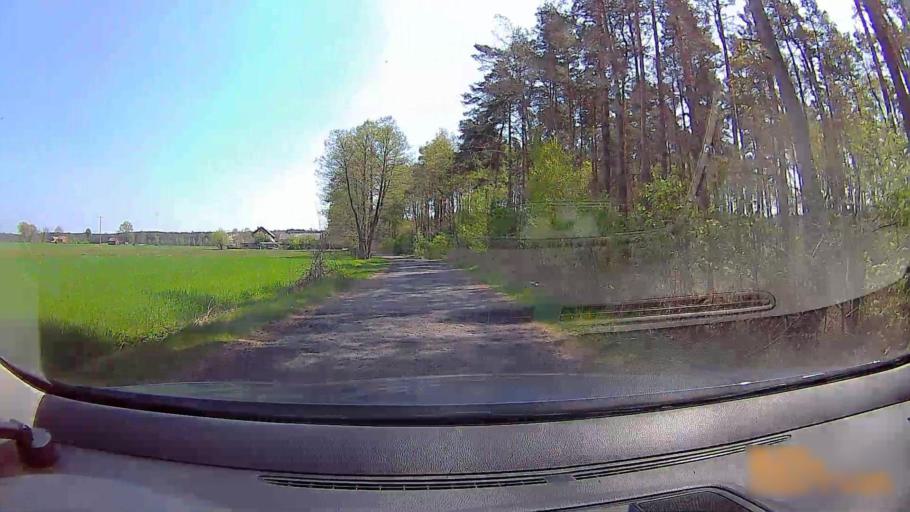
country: PL
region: Greater Poland Voivodeship
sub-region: Powiat koninski
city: Rychwal
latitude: 52.0927
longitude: 18.1771
